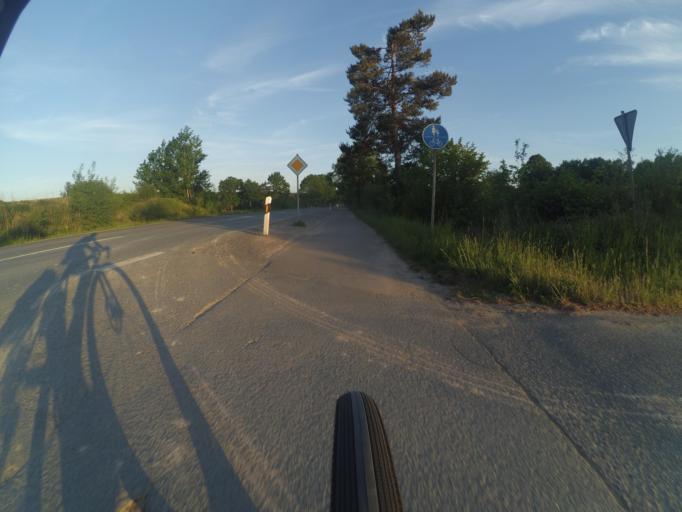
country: DE
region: North Rhine-Westphalia
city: Ibbenburen
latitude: 52.3230
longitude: 7.6703
